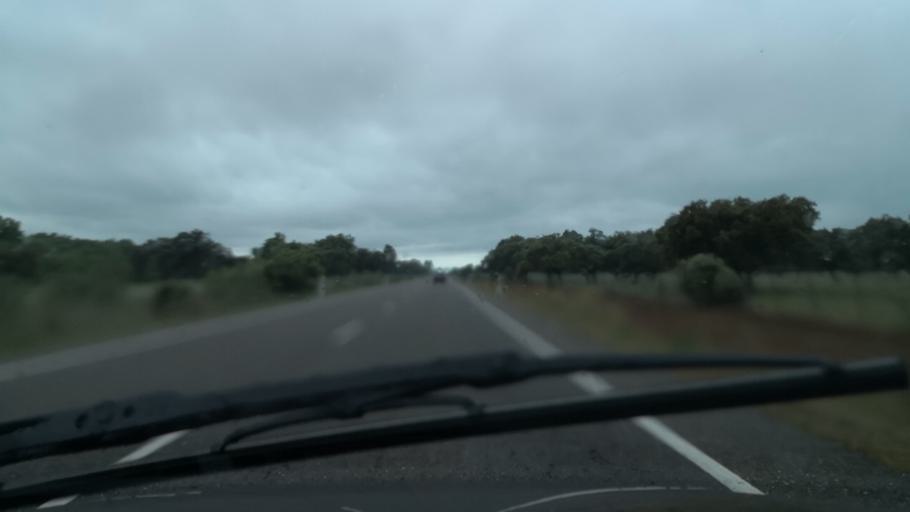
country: ES
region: Extremadura
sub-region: Provincia de Badajoz
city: La Roca de la Sierra
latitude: 39.0869
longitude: -6.7292
